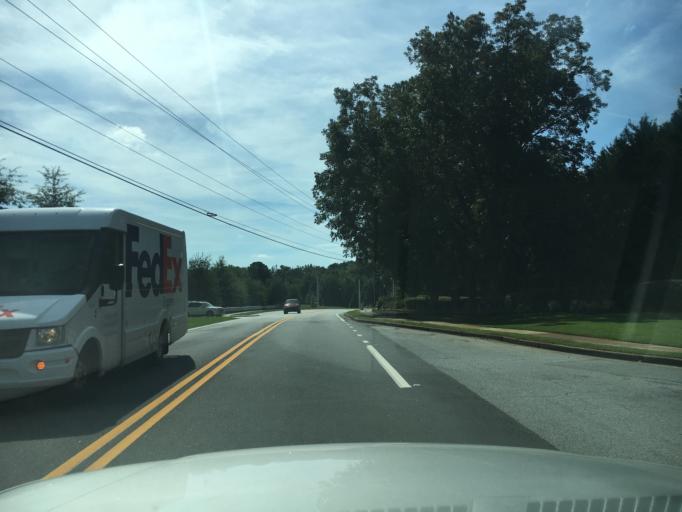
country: US
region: Georgia
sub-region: Gwinnett County
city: Duluth
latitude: 33.9864
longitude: -84.1005
